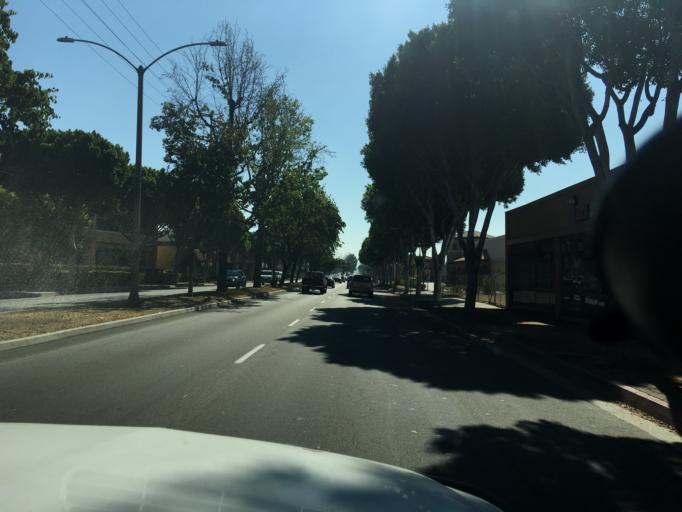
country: US
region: California
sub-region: Los Angeles County
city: North El Monte
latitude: 34.1078
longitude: -118.0270
